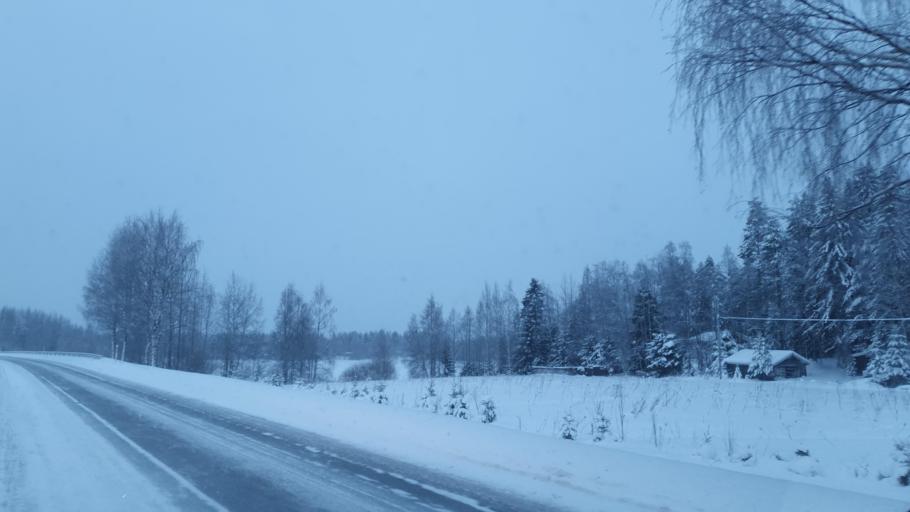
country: FI
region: Kainuu
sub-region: Kajaani
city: Vaala
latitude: 64.5504
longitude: 27.1618
